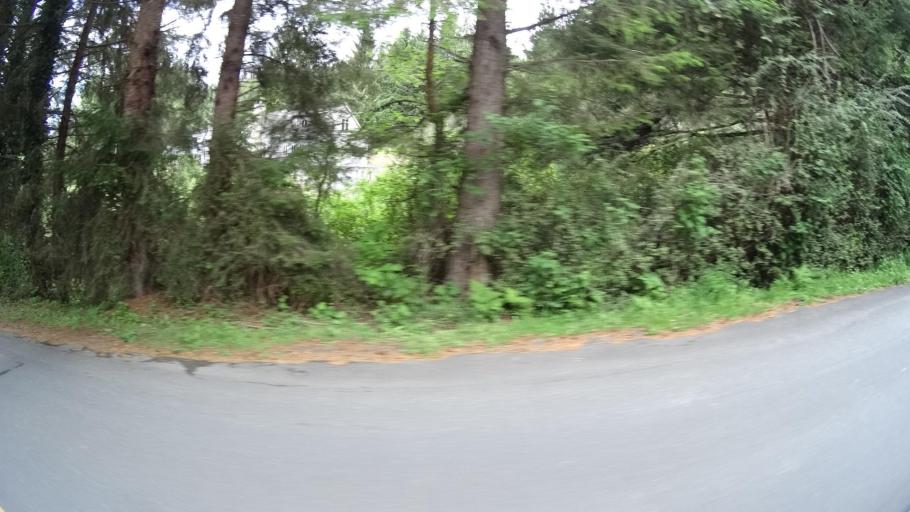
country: US
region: California
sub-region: Humboldt County
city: Bayside
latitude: 40.8526
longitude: -124.0540
